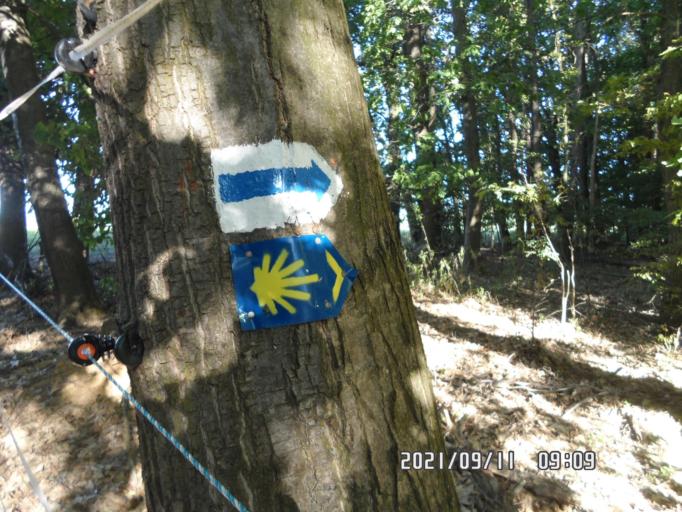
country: HU
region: Zala
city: Zalaegerszeg
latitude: 46.7045
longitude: 16.7424
